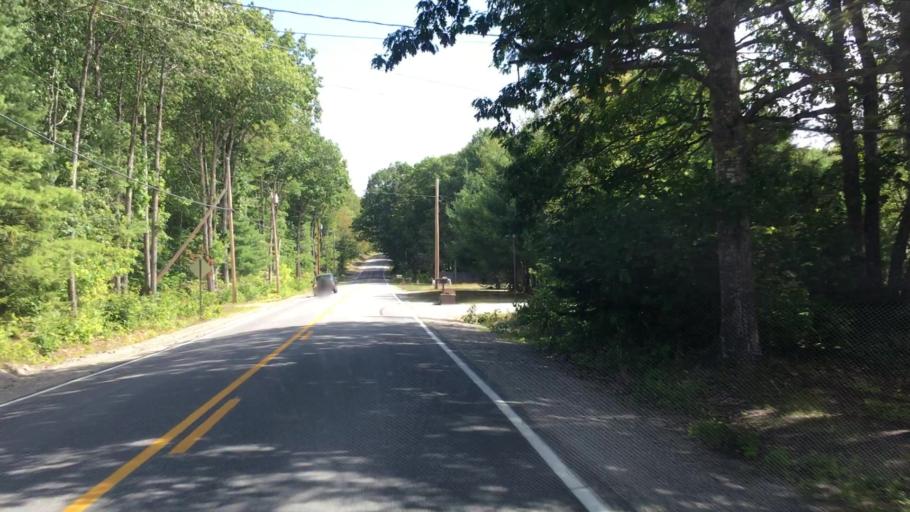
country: US
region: Maine
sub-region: Penobscot County
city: Holden
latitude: 44.7938
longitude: -68.5230
